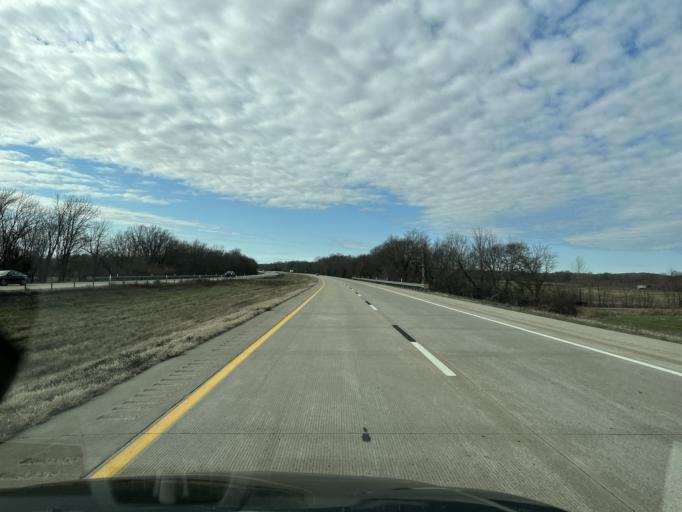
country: US
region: Oklahoma
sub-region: Sequoyah County
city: Sallisaw
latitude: 35.4557
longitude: -94.8482
